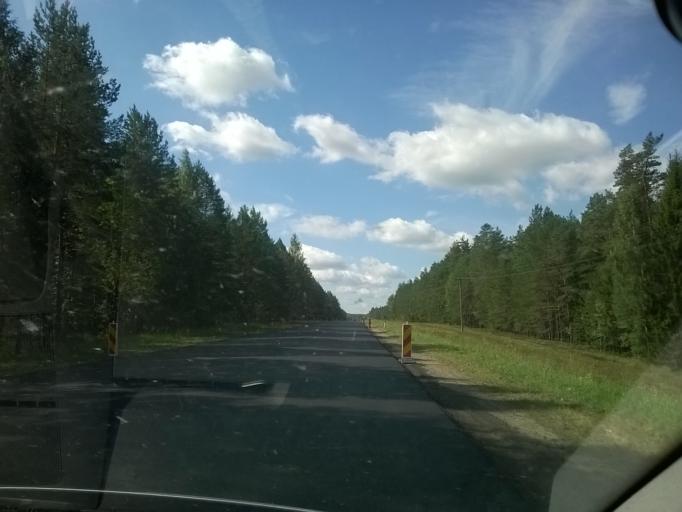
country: EE
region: Vorumaa
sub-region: Voru linn
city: Voru
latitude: 57.8066
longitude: 26.9675
